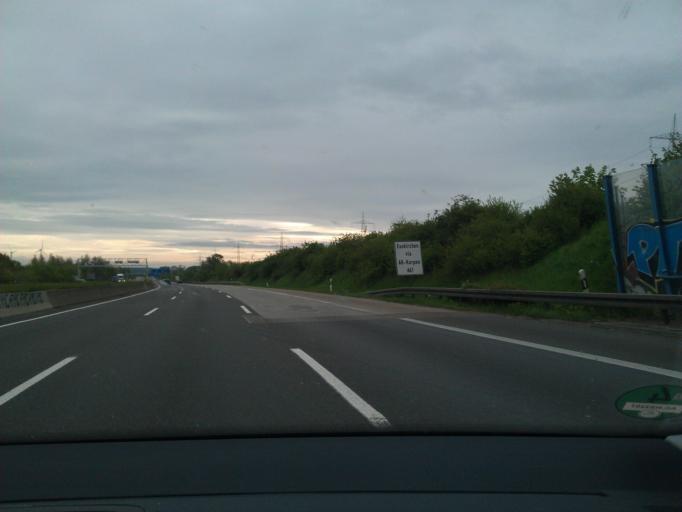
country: DE
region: North Rhine-Westphalia
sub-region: Regierungsbezirk Koln
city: Niederzier
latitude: 50.8357
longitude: 6.4381
